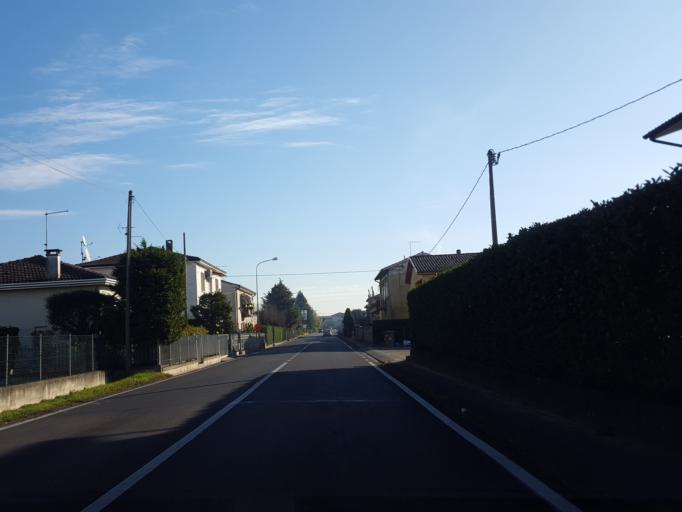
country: IT
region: Veneto
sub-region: Provincia di Vicenza
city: Grumolo delle Abbadesse
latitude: 45.5212
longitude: 11.6522
